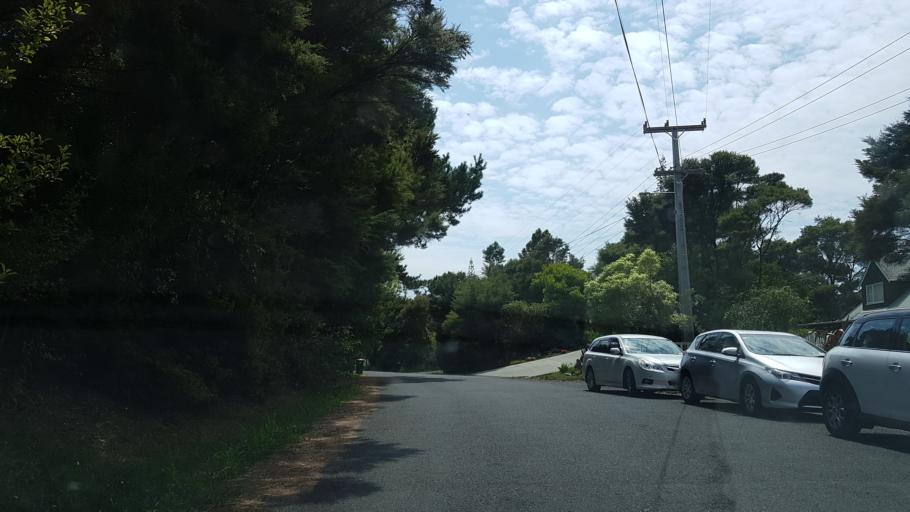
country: NZ
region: Auckland
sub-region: Auckland
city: North Shore
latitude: -36.7827
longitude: 174.6775
